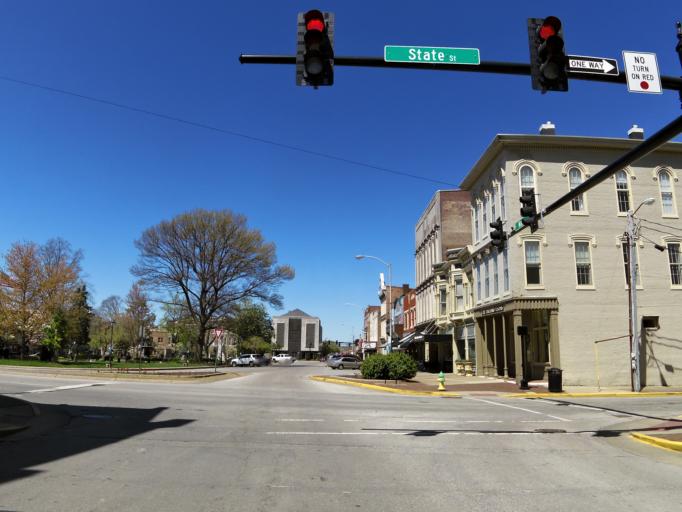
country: US
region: Kentucky
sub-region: Warren County
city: Bowling Green
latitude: 36.9928
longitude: -86.4404
